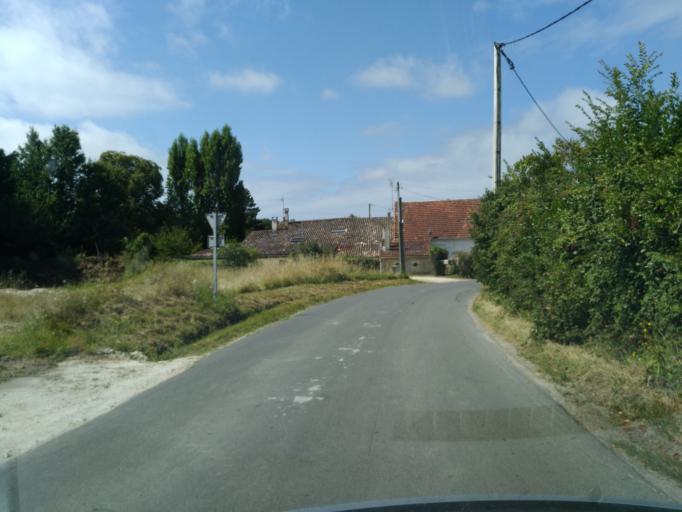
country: FR
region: Poitou-Charentes
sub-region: Departement de la Charente-Maritime
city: Breuillet
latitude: 45.6953
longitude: -1.0672
